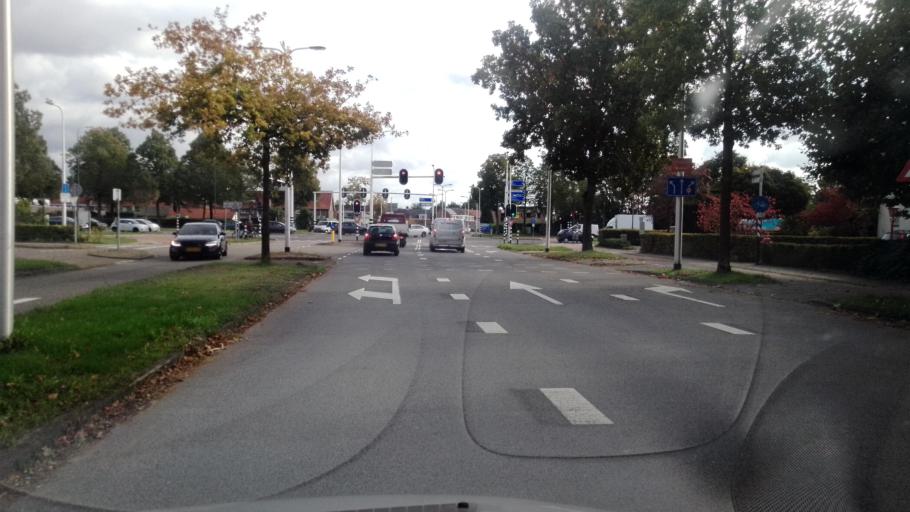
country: NL
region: North Brabant
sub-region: Gemeente Helmond
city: Helmond
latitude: 51.4752
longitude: 5.6324
